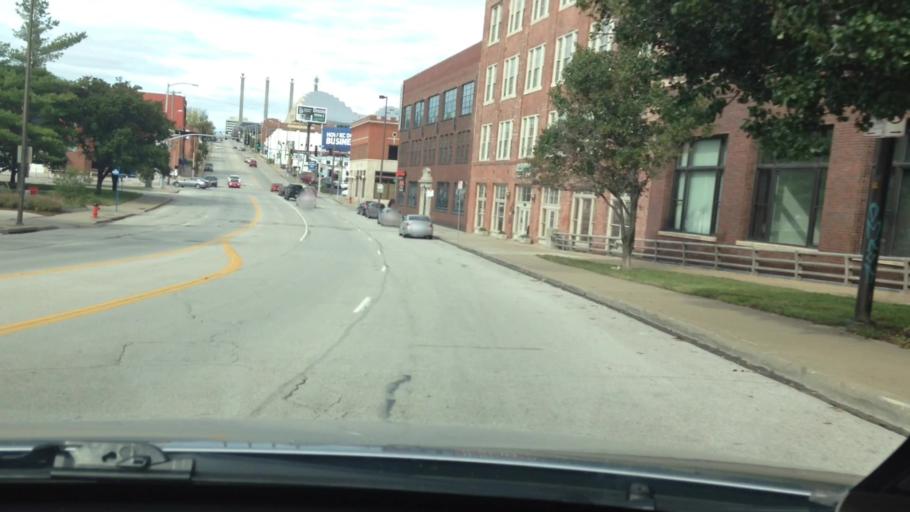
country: US
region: Missouri
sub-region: Jackson County
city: Kansas City
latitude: 39.0865
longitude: -94.5891
